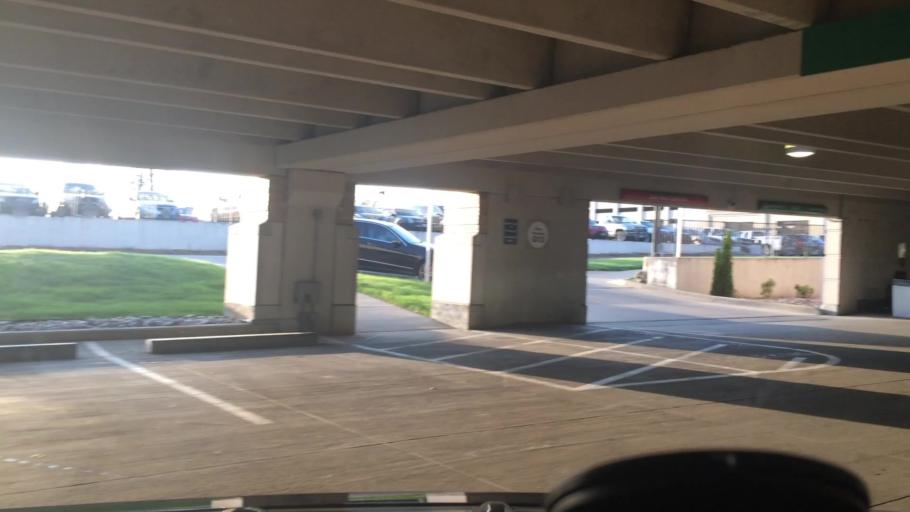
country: US
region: Missouri
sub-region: Greene County
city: Springfield
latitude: 37.1816
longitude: -93.2751
